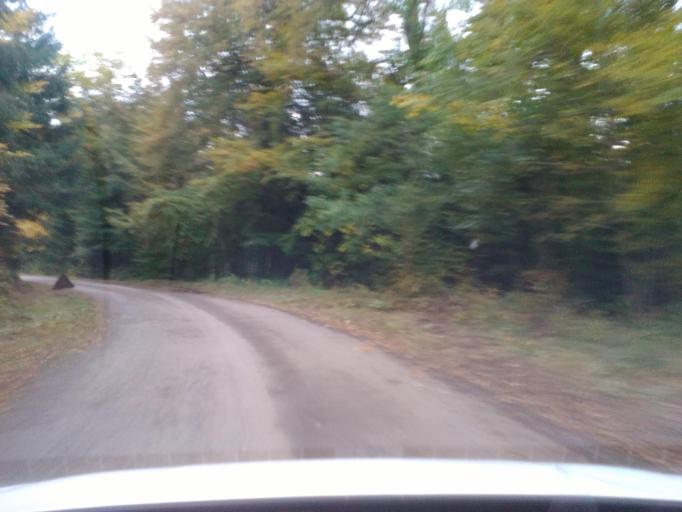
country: FR
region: Lorraine
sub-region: Departement des Vosges
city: Senones
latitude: 48.3779
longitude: 7.0840
